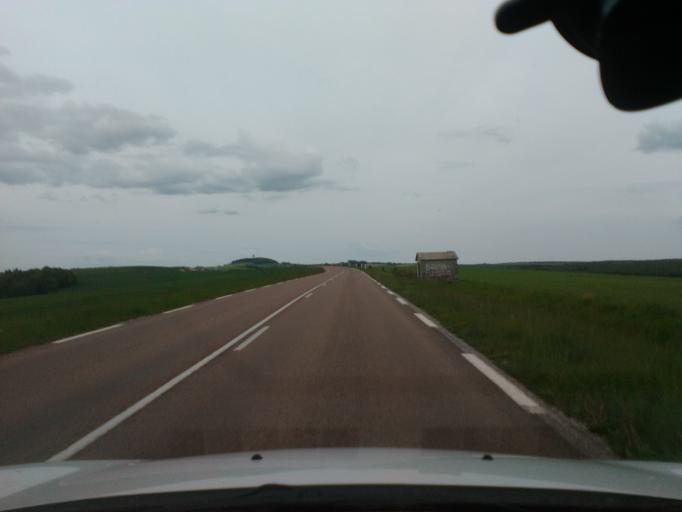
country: FR
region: Champagne-Ardenne
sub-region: Departement de l'Aube
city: Ville-sous-la-Ferte
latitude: 48.2171
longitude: 4.8261
